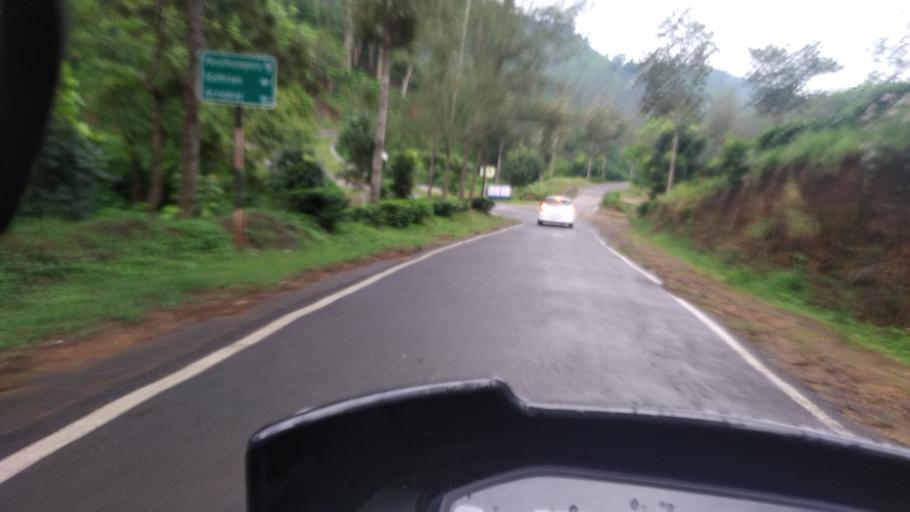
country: IN
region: Tamil Nadu
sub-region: Theni
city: Gudalur
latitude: 9.5662
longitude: 77.0780
